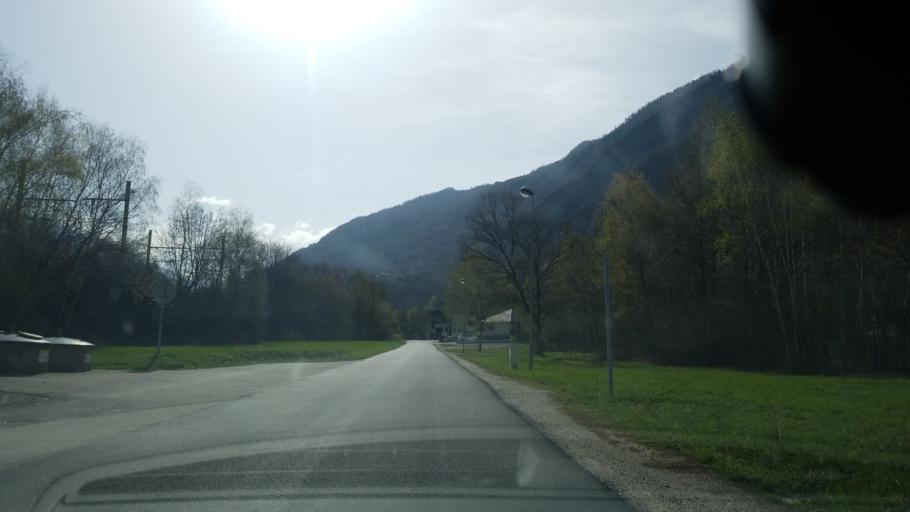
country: FR
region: Rhone-Alpes
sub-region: Departement de la Savoie
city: Villargondran
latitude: 45.2531
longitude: 6.3872
